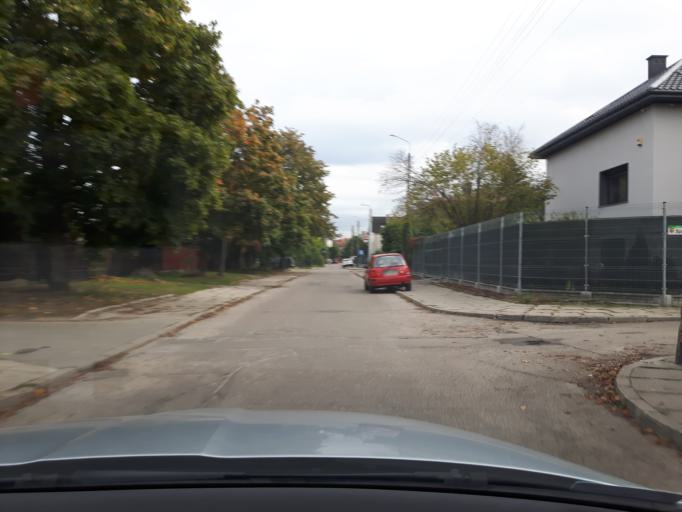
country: PL
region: Masovian Voivodeship
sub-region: Powiat wolominski
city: Zabki
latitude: 52.2896
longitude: 21.1233
